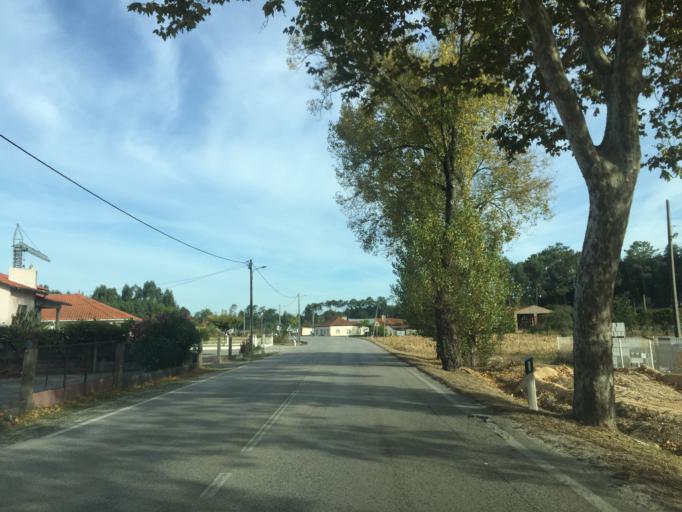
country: PT
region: Leiria
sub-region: Pombal
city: Lourical
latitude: 39.9573
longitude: -8.7865
